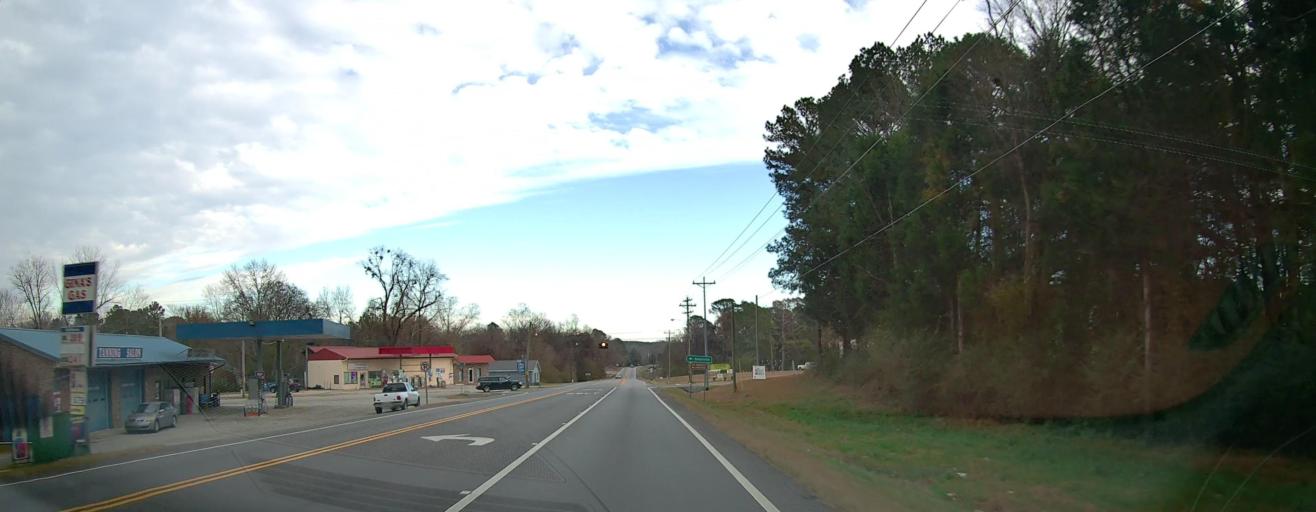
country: US
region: Alabama
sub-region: Morgan County
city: Priceville
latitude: 34.4709
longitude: -86.7990
